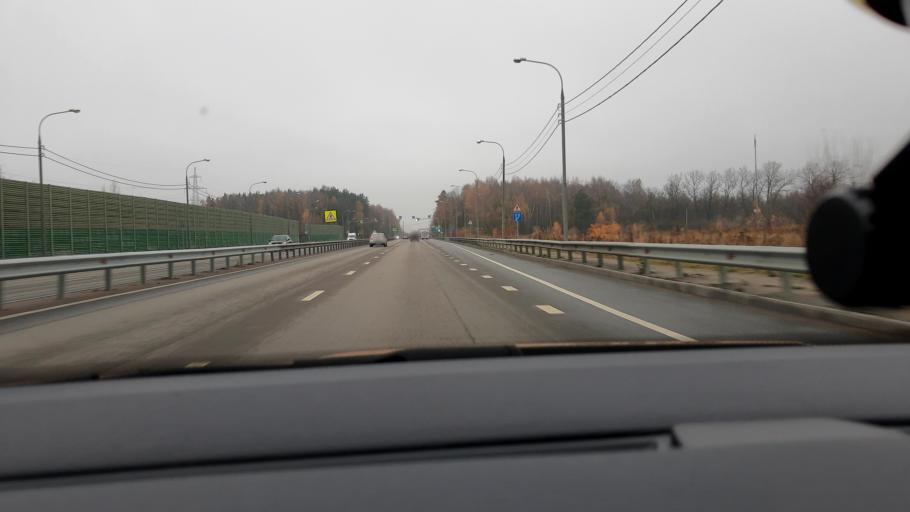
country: RU
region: Moscow
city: Vatutino
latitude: 55.9355
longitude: 37.6573
